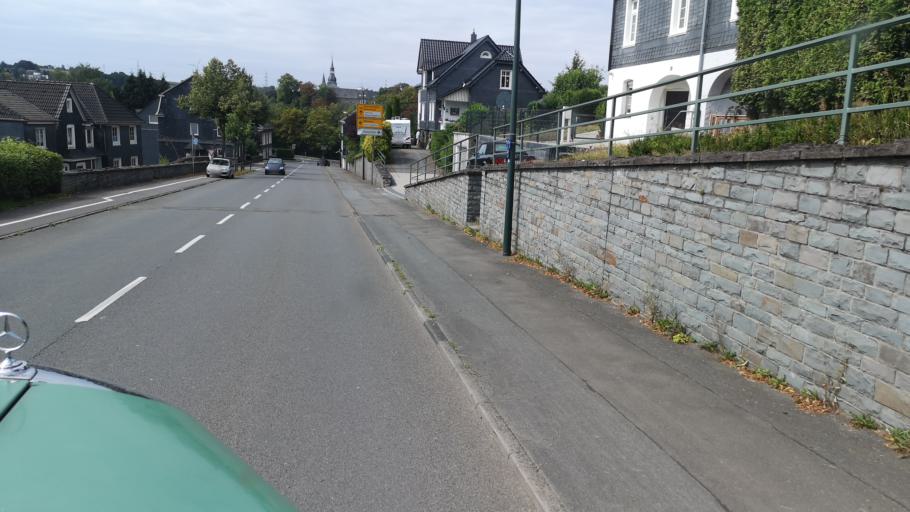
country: DE
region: North Rhine-Westphalia
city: Huckeswagen
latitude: 51.1536
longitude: 7.3469
